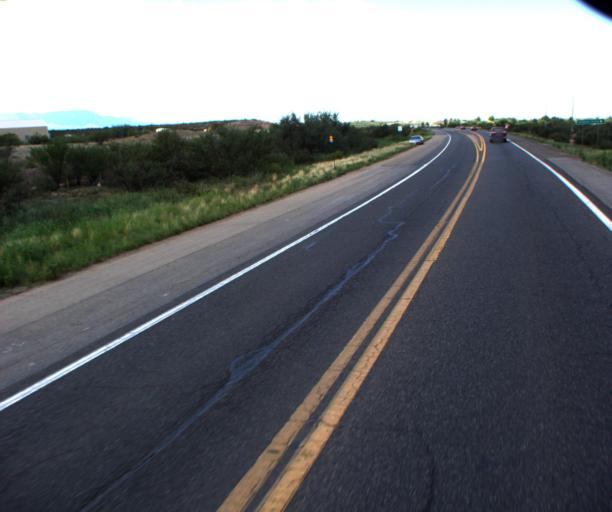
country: US
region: Arizona
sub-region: Yavapai County
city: Camp Verde
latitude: 34.5895
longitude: -111.8880
